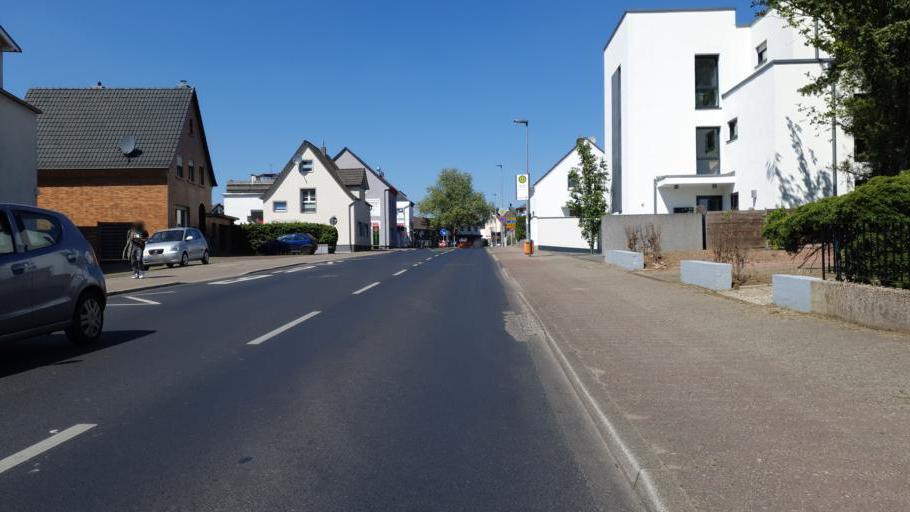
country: DE
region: North Rhine-Westphalia
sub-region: Regierungsbezirk Koln
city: Odenthal
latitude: 51.0127
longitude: 7.0804
